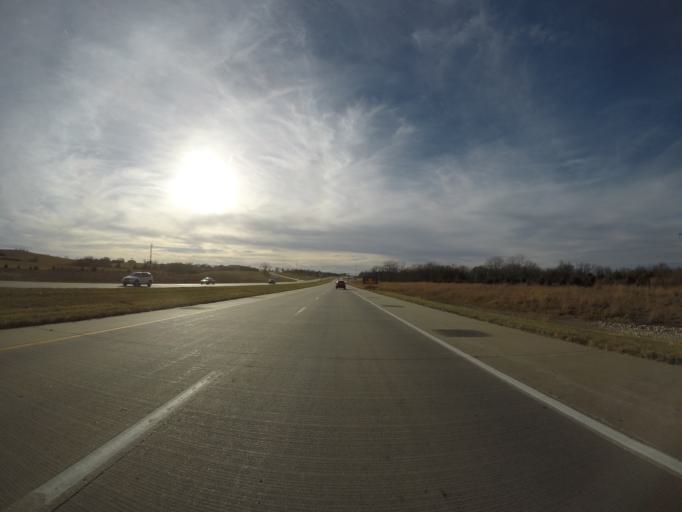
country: US
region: Kansas
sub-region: Franklin County
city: Ottawa
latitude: 38.5729
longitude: -95.2777
